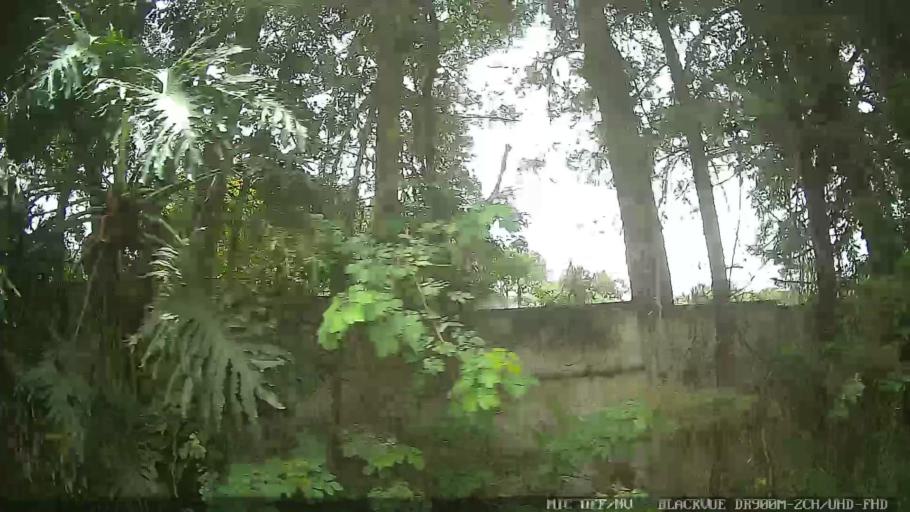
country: BR
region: Sao Paulo
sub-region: Santa Isabel
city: Santa Isabel
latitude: -23.3384
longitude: -46.2173
